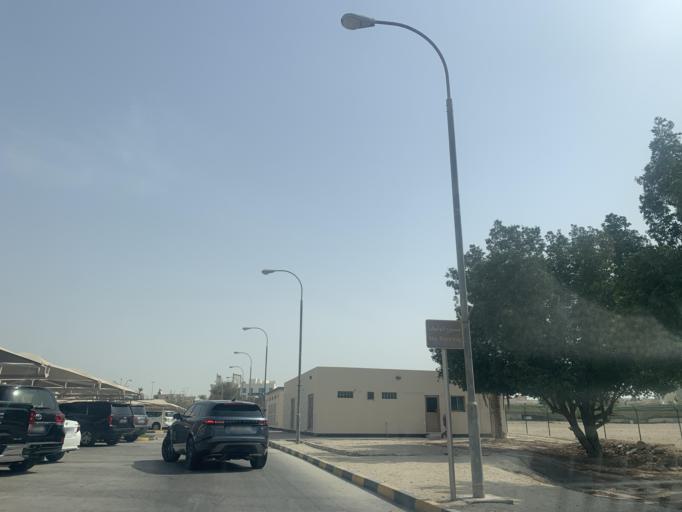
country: BH
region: Northern
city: Ar Rifa'
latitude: 26.1324
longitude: 50.5507
